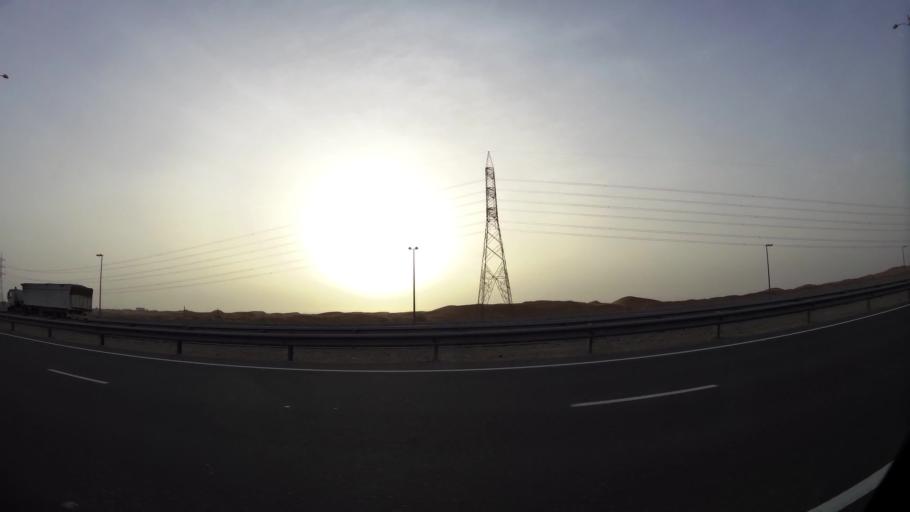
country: OM
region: Al Buraimi
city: Al Buraymi
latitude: 24.3448
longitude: 55.7767
